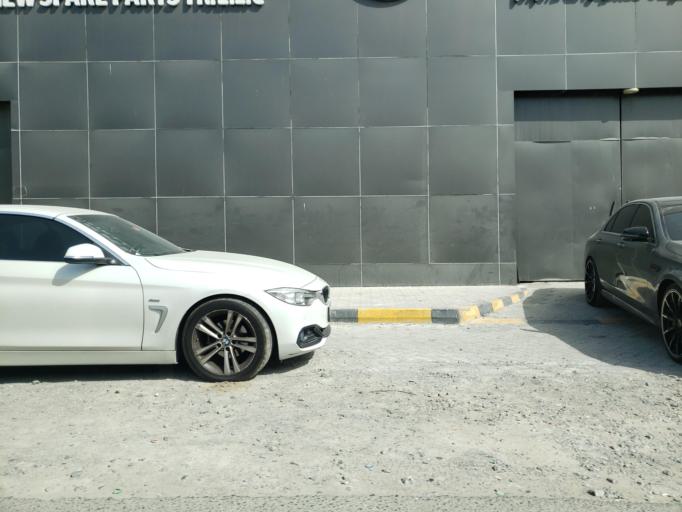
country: AE
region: Ash Shariqah
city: Sharjah
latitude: 25.3289
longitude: 55.4018
